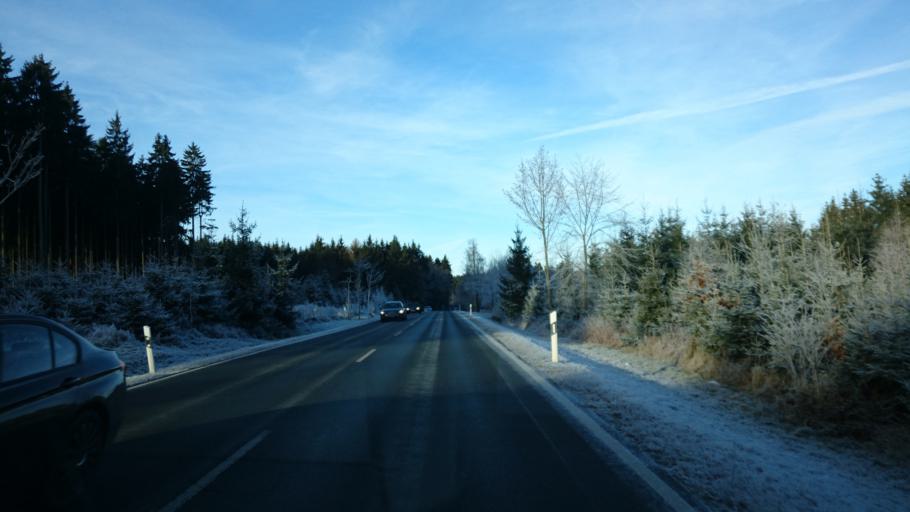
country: DE
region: Thuringia
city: Schleiz
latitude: 50.5487
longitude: 11.8469
